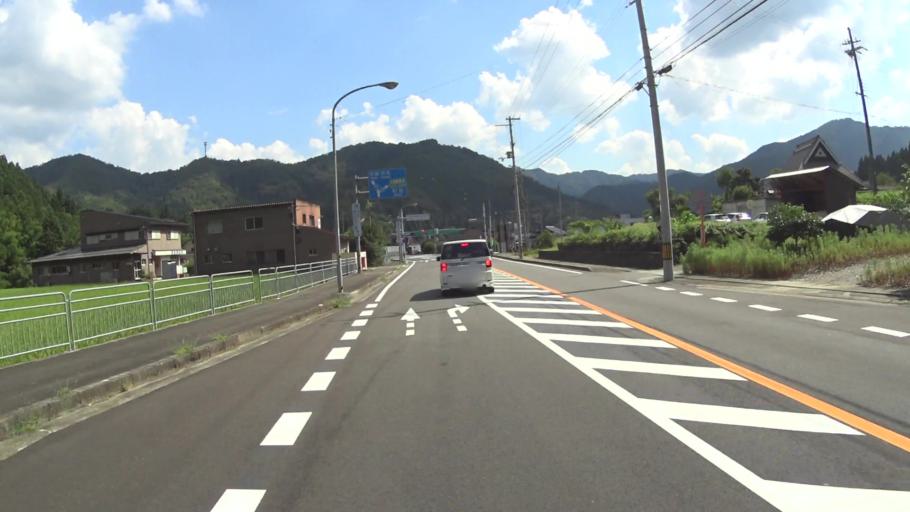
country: JP
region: Kyoto
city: Maizuru
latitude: 35.2791
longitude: 135.5545
